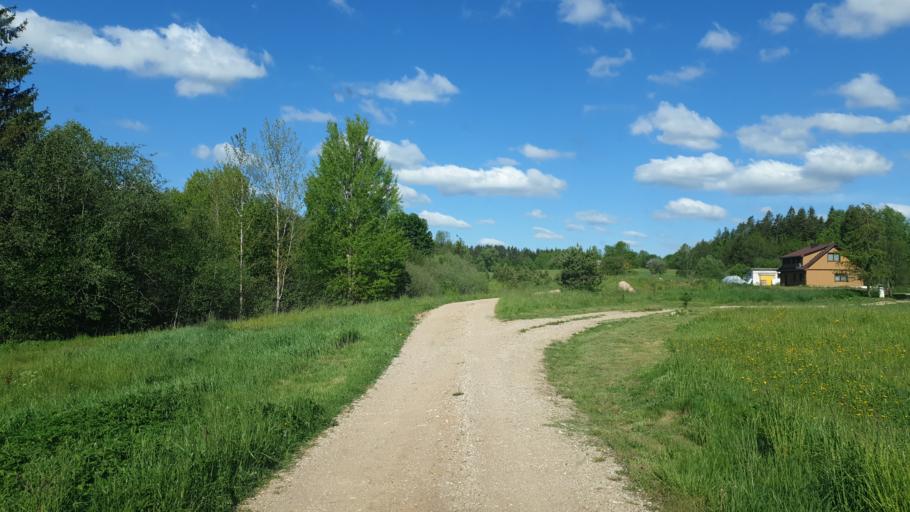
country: LT
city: Aukstadvaris
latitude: 54.5808
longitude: 24.4578
